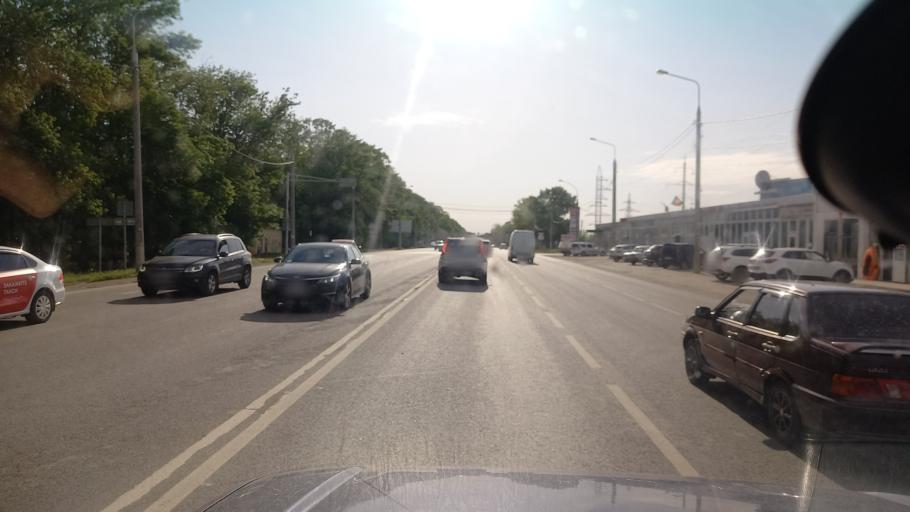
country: RU
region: Krasnodarskiy
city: Krasnodar
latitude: 45.0564
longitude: 38.8950
